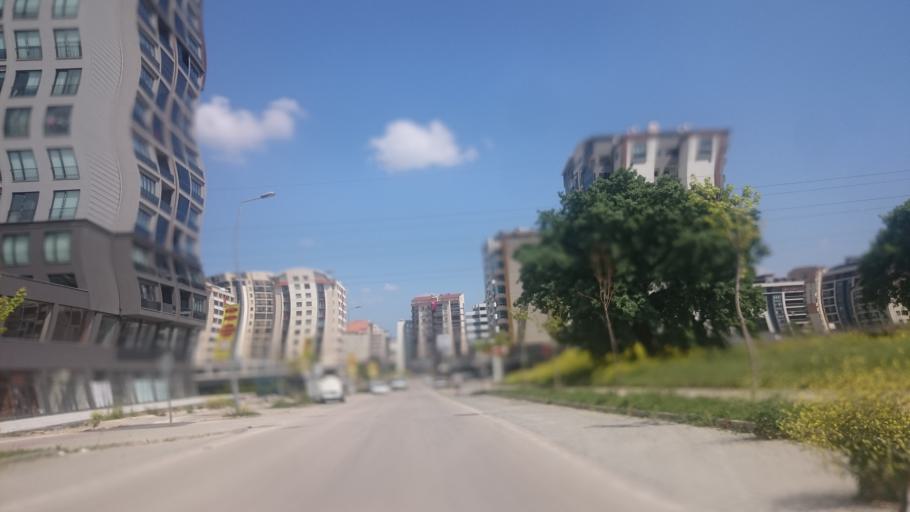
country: TR
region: Bursa
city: Cali
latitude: 40.2169
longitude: 28.9454
